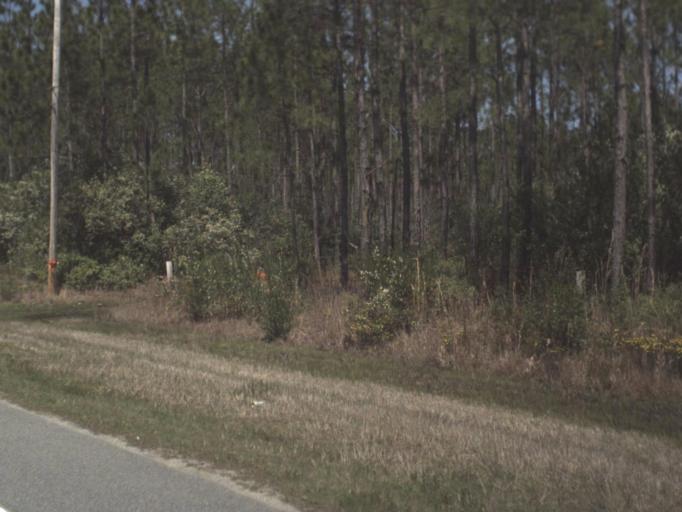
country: US
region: Florida
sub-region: Bay County
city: Lynn Haven
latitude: 30.3302
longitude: -85.7465
